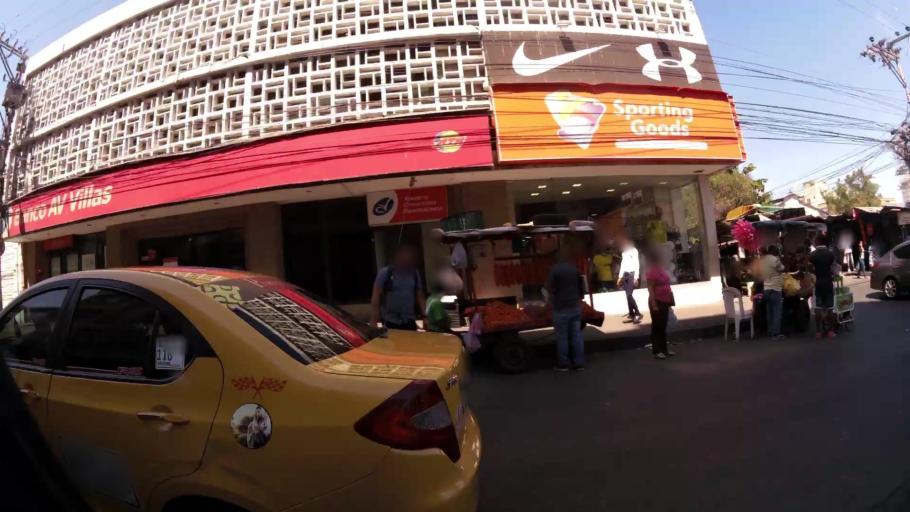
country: CO
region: Atlantico
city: Barranquilla
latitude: 10.9819
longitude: -74.7815
